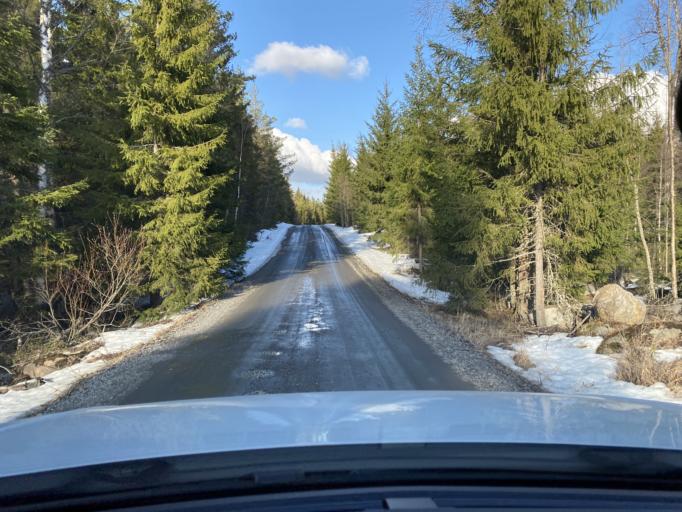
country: FI
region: Pirkanmaa
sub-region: Lounais-Pirkanmaa
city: Mouhijaervi
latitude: 61.4545
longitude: 22.9289
